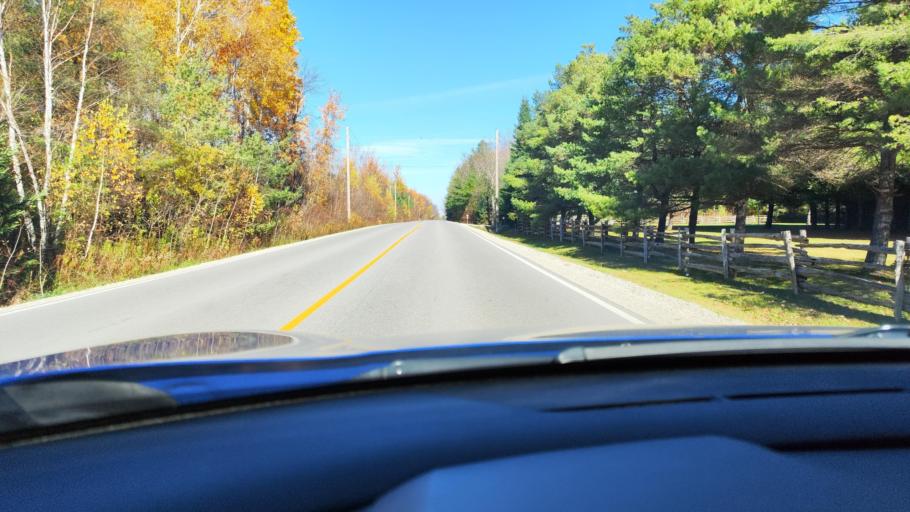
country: CA
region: Ontario
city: Wasaga Beach
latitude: 44.4057
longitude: -80.0590
